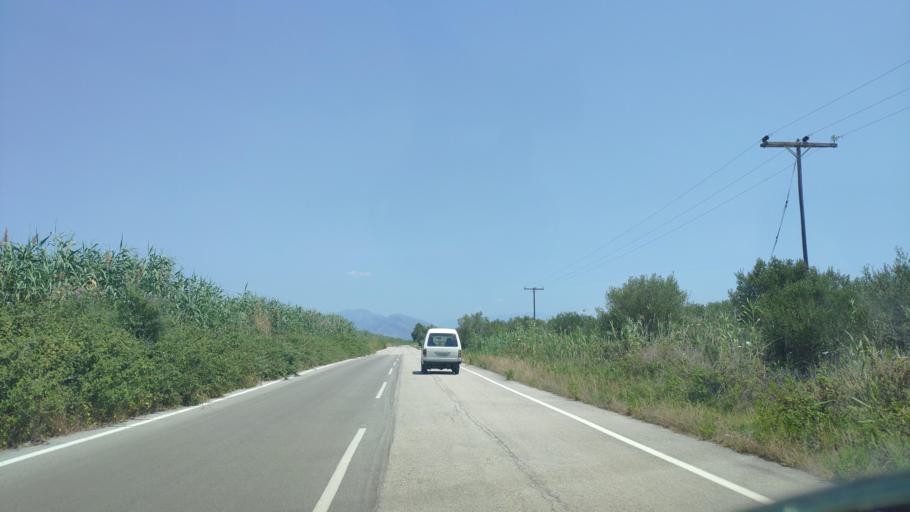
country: GR
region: Epirus
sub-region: Nomos Artas
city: Aneza
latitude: 39.0520
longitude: 20.8631
